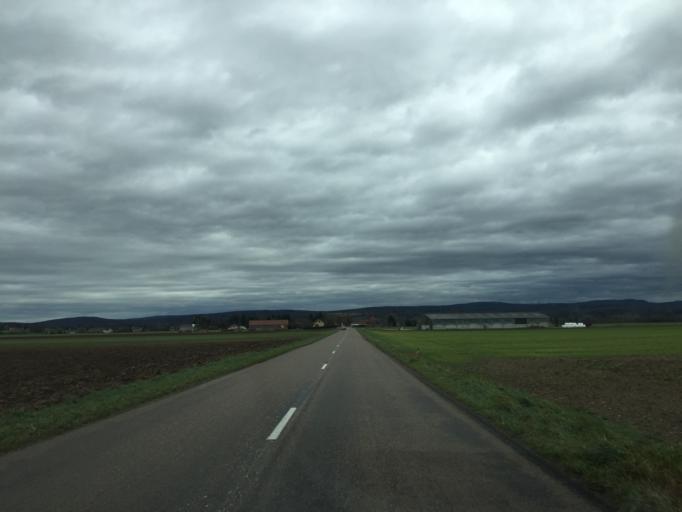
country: FR
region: Franche-Comte
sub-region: Departement du Doubs
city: Arc-et-Senans
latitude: 47.0281
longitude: 5.7515
